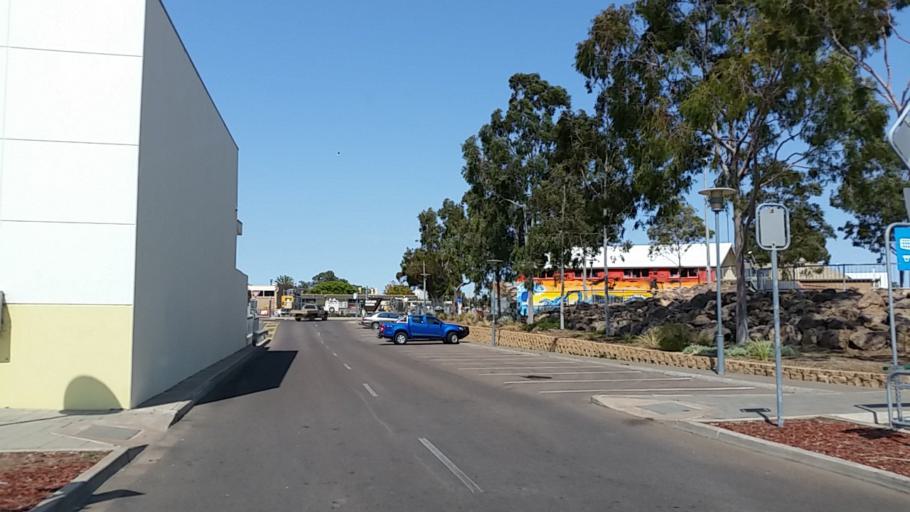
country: AU
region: South Australia
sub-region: Port Augusta
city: Port Augusta West
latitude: -32.4908
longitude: 137.7597
